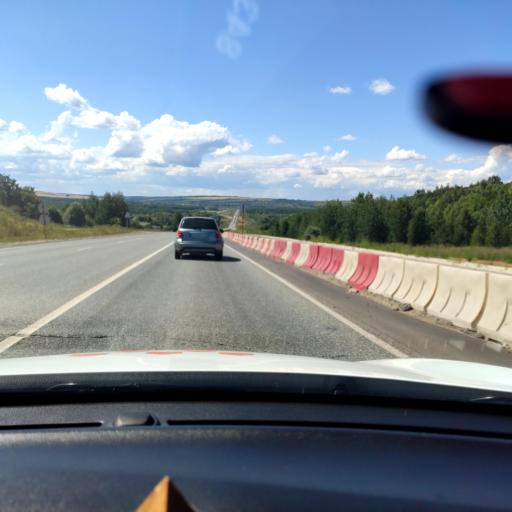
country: RU
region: Tatarstan
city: Sviyazhsk
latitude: 55.7172
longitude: 48.7270
